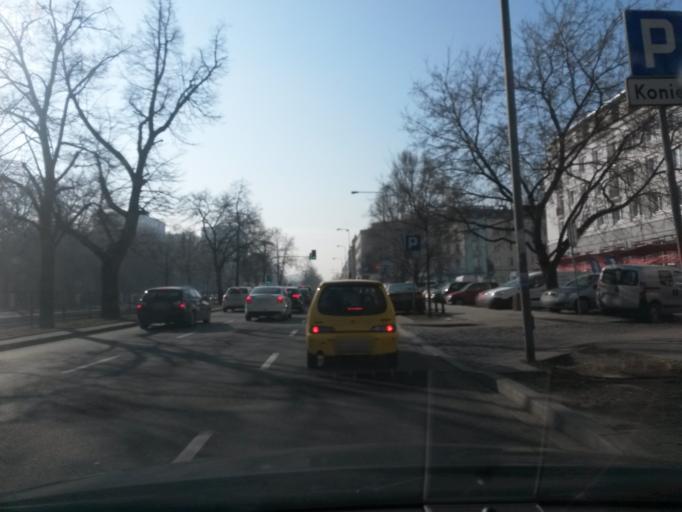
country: PL
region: Masovian Voivodeship
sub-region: Warszawa
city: Mokotow
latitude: 52.1955
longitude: 21.0240
